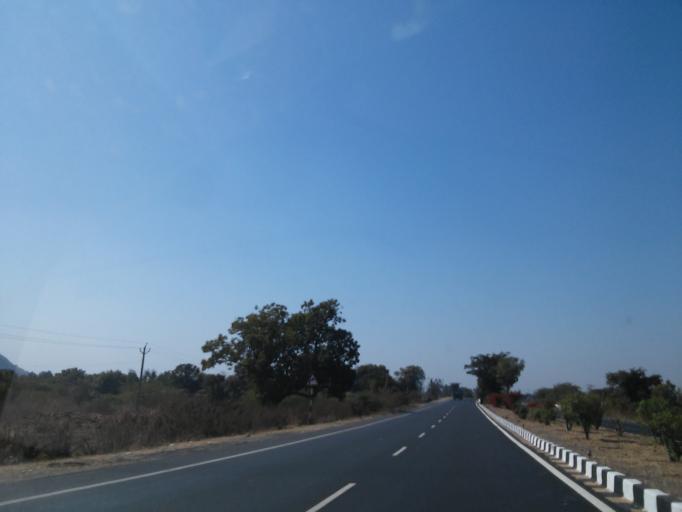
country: IN
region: Gujarat
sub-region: Sabar Kantha
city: Modasa
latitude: 23.6066
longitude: 73.2286
